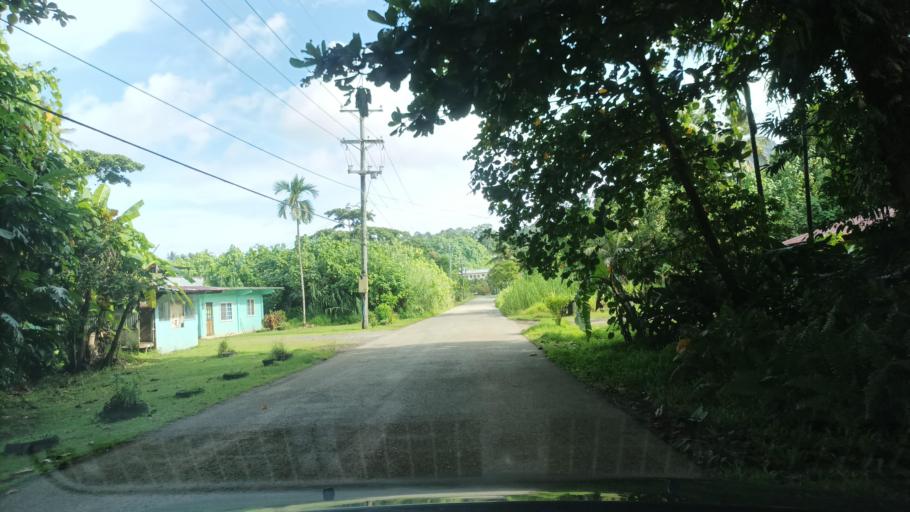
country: FM
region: Kosrae
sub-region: Lelu Municipality
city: Tofol
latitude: 5.3306
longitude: 163.0081
